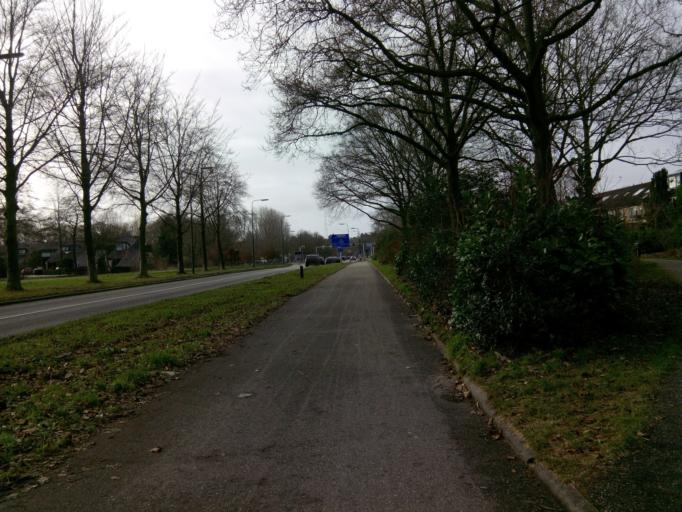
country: NL
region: Utrecht
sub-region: Gemeente Leusden
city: Leusden
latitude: 52.1329
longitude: 5.4199
